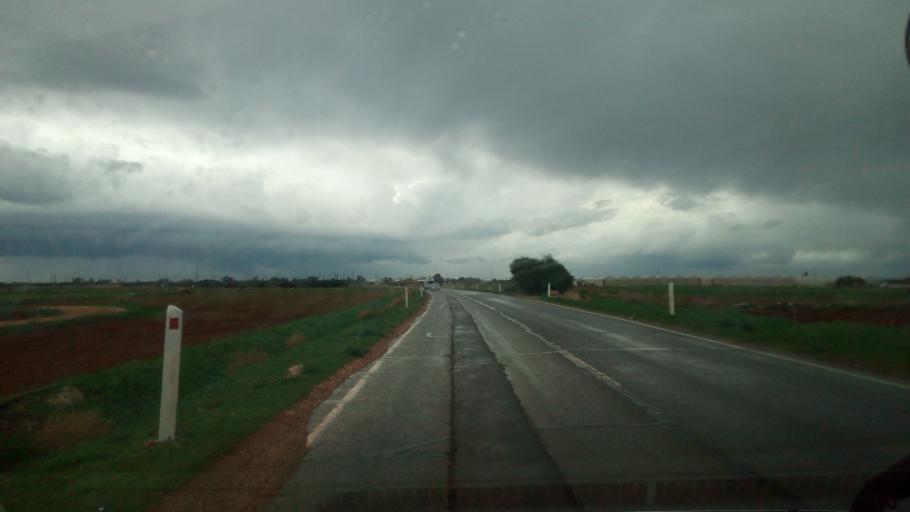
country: CY
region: Ammochostos
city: Liopetri
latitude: 34.9831
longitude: 33.8948
